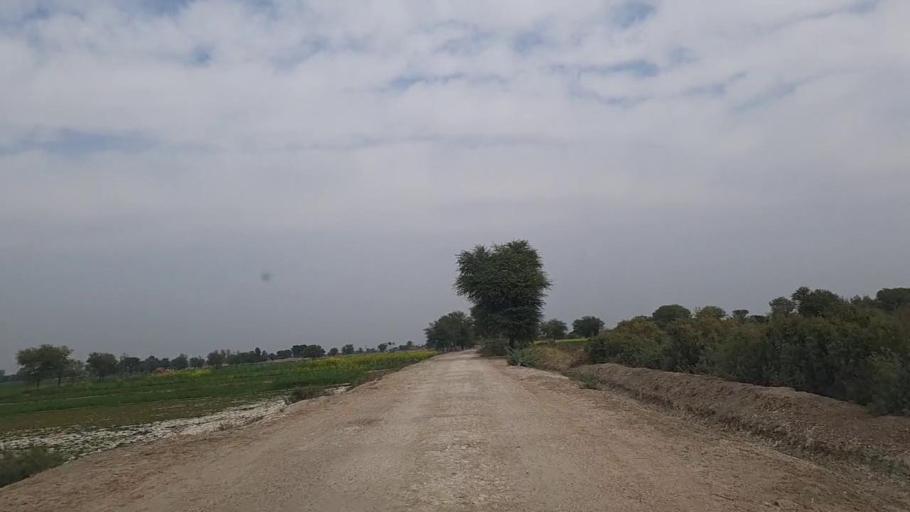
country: PK
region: Sindh
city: Daur
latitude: 26.4292
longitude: 68.4631
